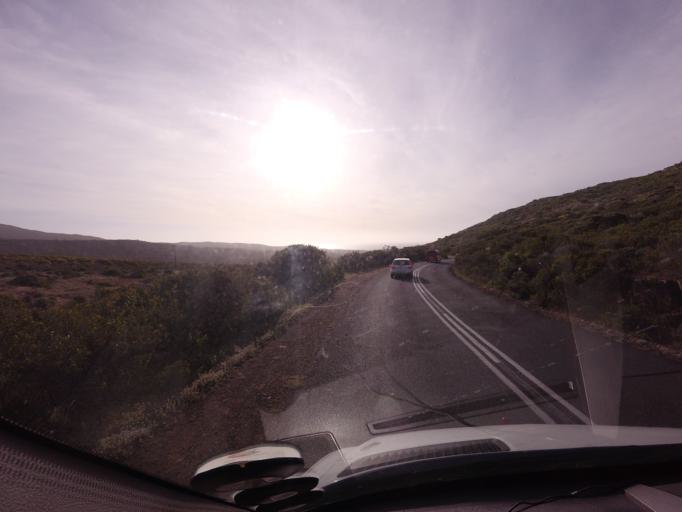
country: ZA
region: Western Cape
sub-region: City of Cape Town
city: Bergvliet
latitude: -34.2048
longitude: 18.3937
